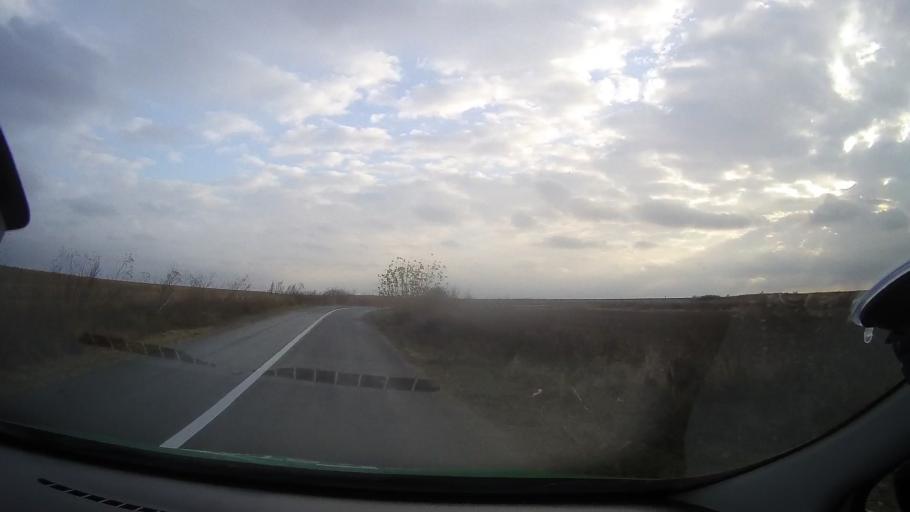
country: RO
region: Constanta
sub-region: Comuna Pestera
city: Pestera
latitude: 44.1341
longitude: 28.1192
